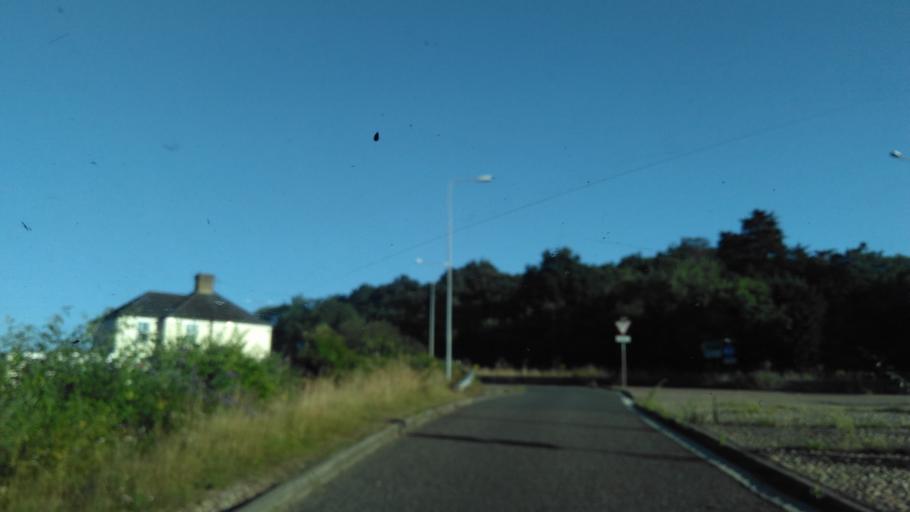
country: GB
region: England
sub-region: Kent
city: Dunkirk
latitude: 51.2883
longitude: 1.0037
